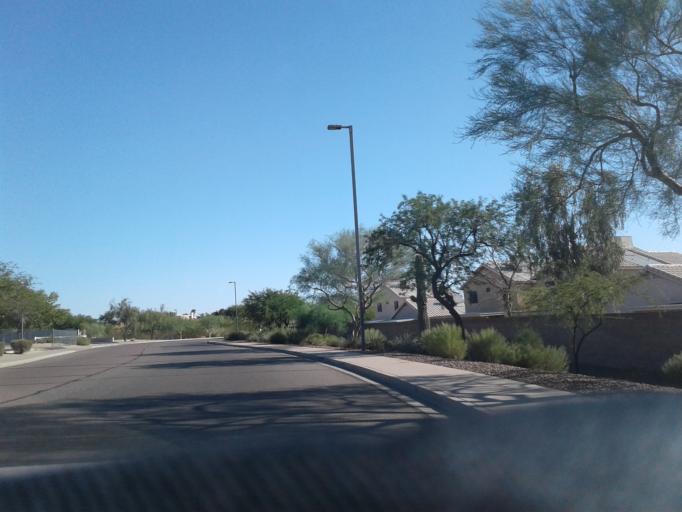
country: US
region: Arizona
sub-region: Maricopa County
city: Cave Creek
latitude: 33.6923
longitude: -112.0362
